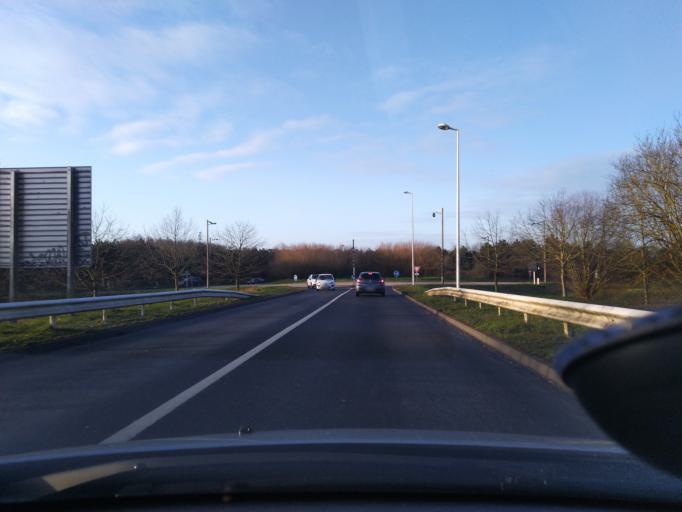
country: FR
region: Haute-Normandie
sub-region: Departement de la Seine-Maritime
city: Maromme
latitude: 49.4804
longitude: 1.0104
